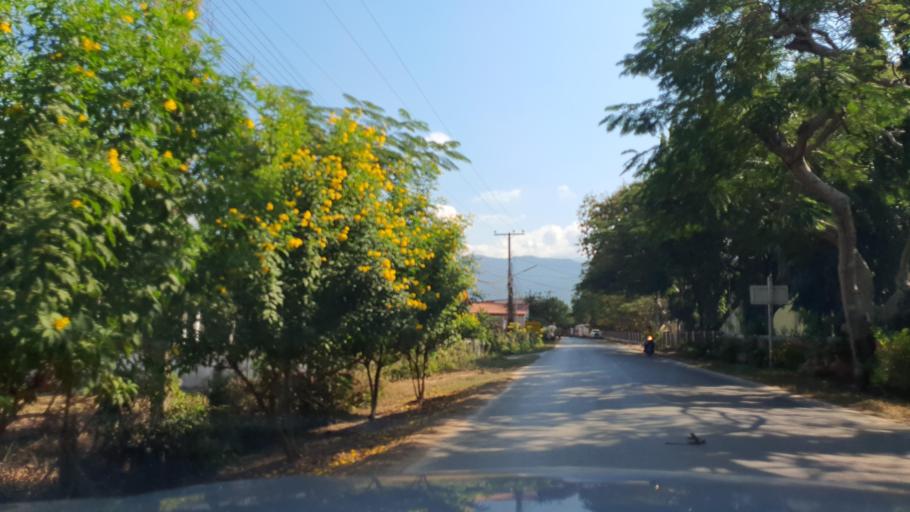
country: TH
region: Nan
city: Pua
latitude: 19.1408
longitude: 100.9306
